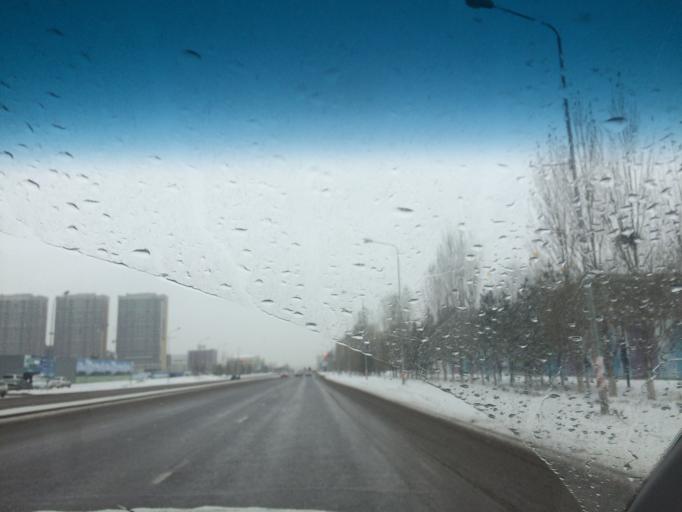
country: KZ
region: Astana Qalasy
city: Astana
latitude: 51.1236
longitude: 71.4203
